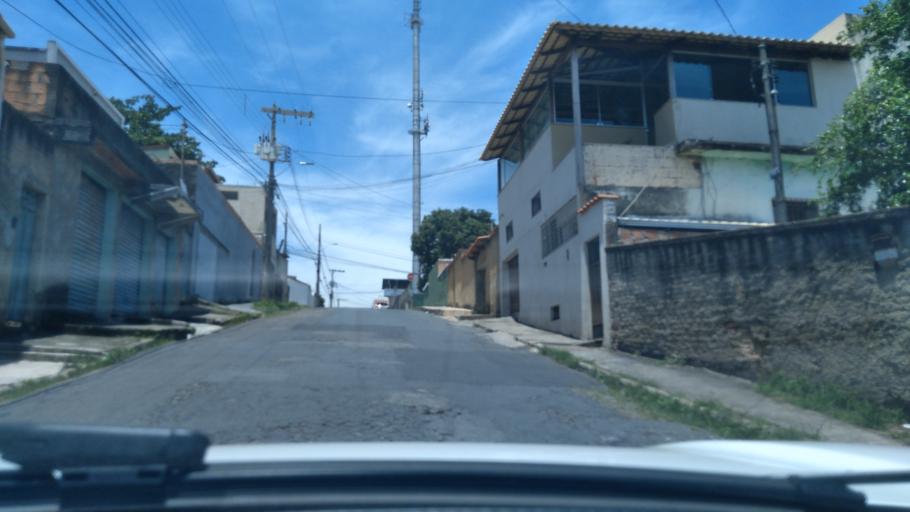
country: BR
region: Minas Gerais
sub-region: Contagem
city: Contagem
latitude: -19.9306
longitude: -43.9974
